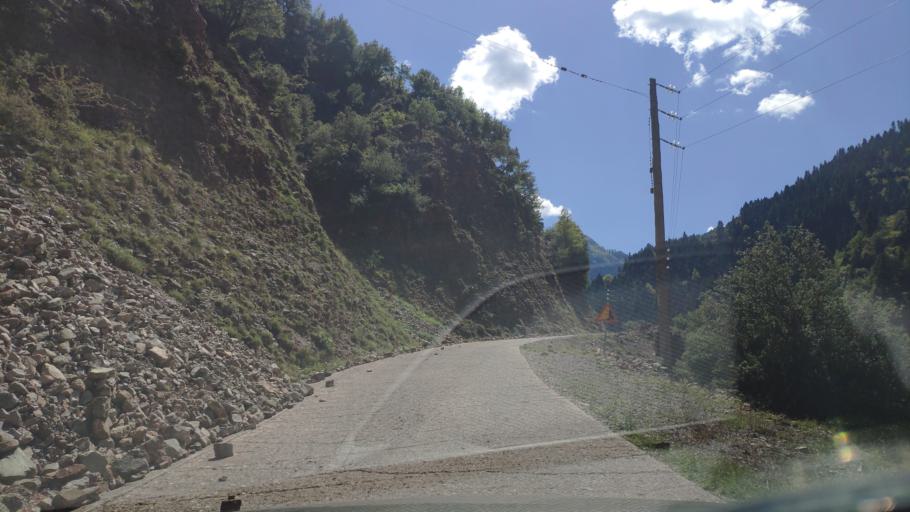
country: GR
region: Central Greece
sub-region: Nomos Evrytanias
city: Kerasochori
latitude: 39.1369
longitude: 21.6446
